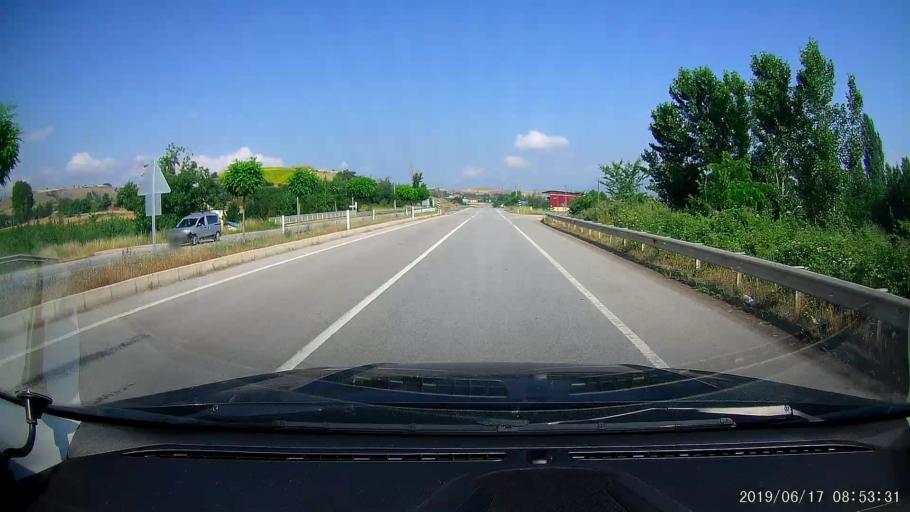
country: TR
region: Tokat
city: Erbaa
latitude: 40.7105
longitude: 36.4801
